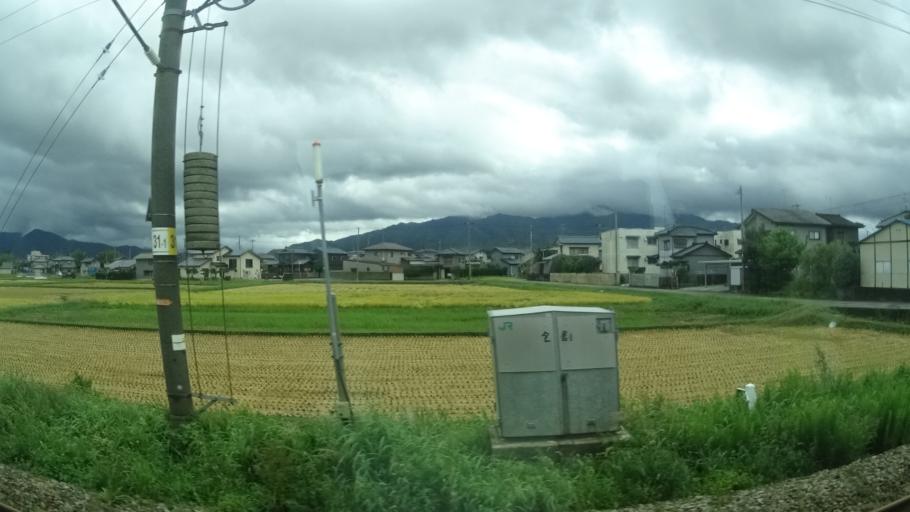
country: JP
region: Niigata
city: Murakami
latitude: 38.1111
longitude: 139.4392
